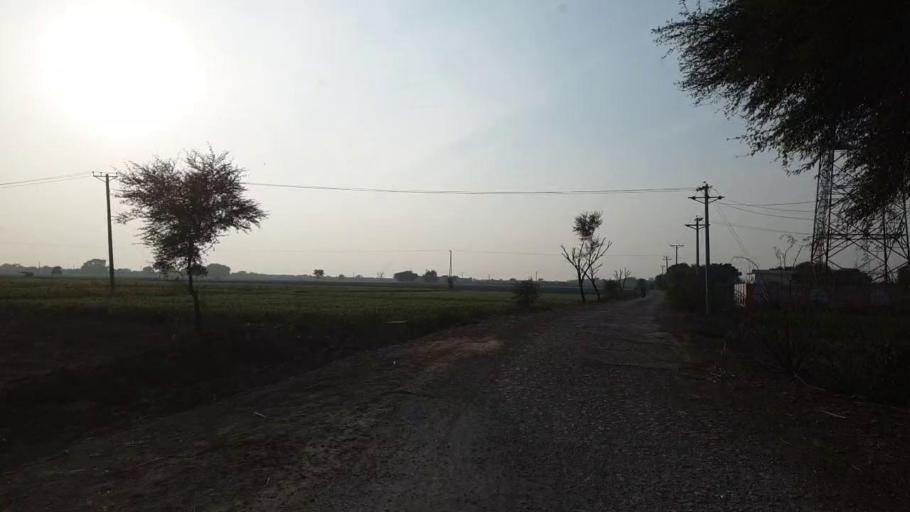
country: PK
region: Sindh
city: Matiari
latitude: 25.5990
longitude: 68.4391
